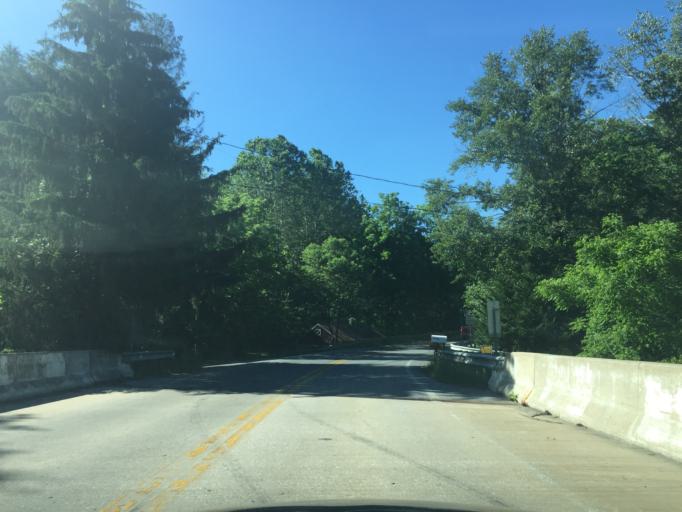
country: US
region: Maryland
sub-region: Carroll County
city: Westminster
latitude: 39.5569
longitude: -76.9181
